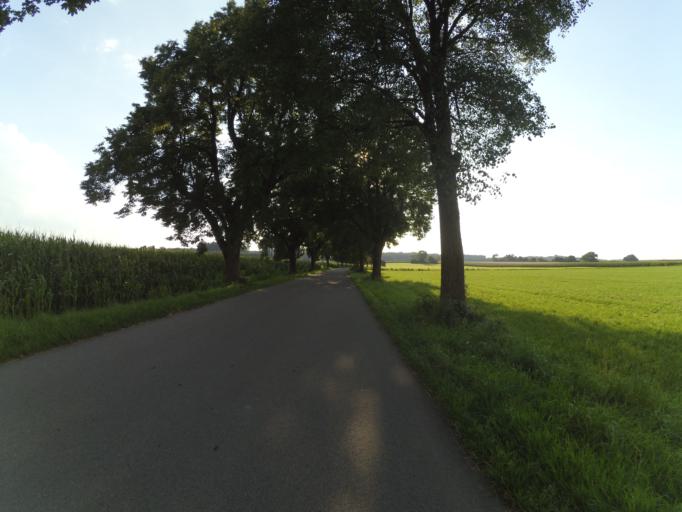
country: DE
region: Bavaria
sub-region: Swabia
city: Tussenhausen
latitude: 48.0664
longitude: 10.5764
